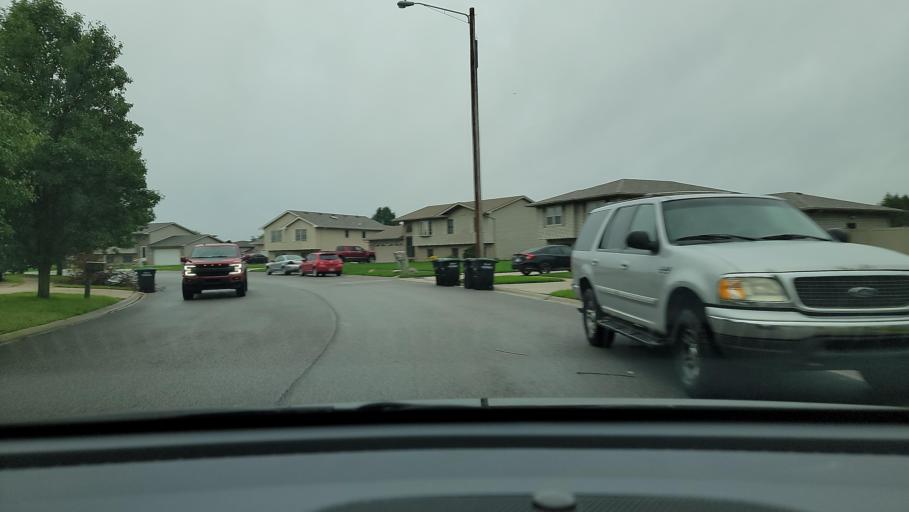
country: US
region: Indiana
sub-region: Porter County
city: Portage
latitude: 41.5641
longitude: -87.1757
